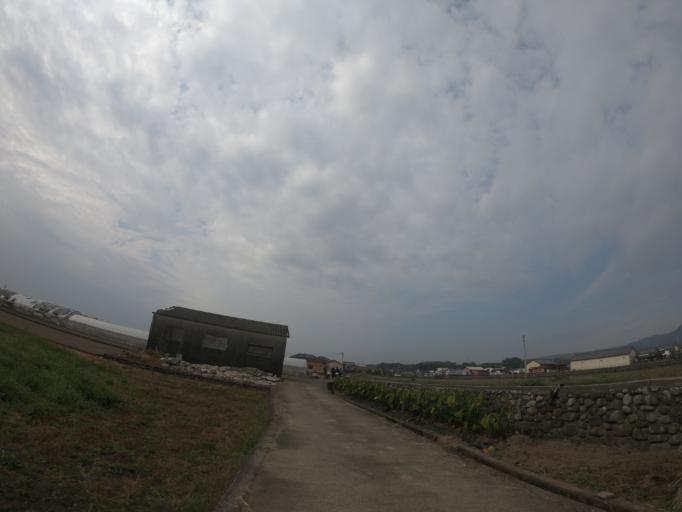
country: JP
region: Nagasaki
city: Shimabara
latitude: 32.6594
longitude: 130.3043
